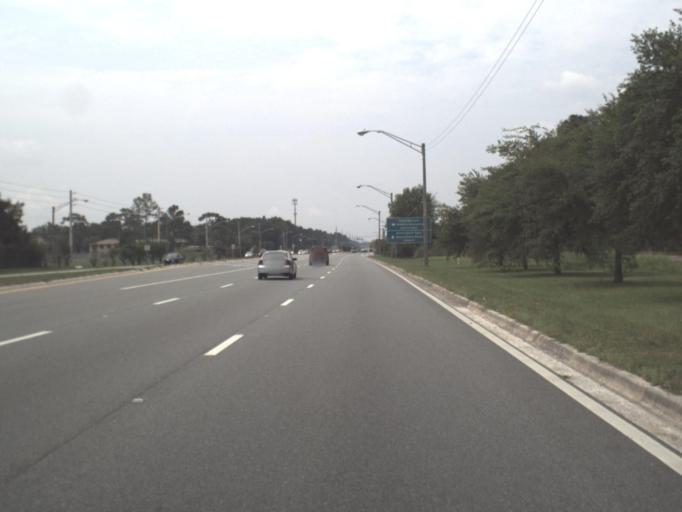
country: US
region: Florida
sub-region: Clay County
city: Orange Park
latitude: 30.2298
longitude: -81.6995
